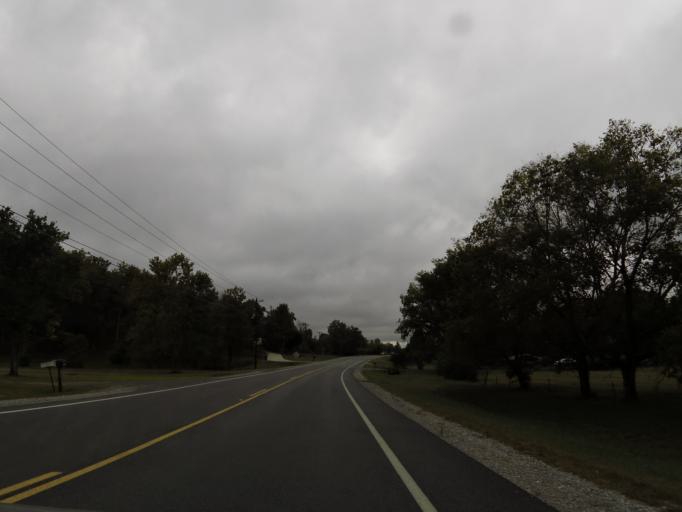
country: US
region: Tennessee
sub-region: Hamilton County
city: Lakesite
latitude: 35.1712
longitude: -85.0293
